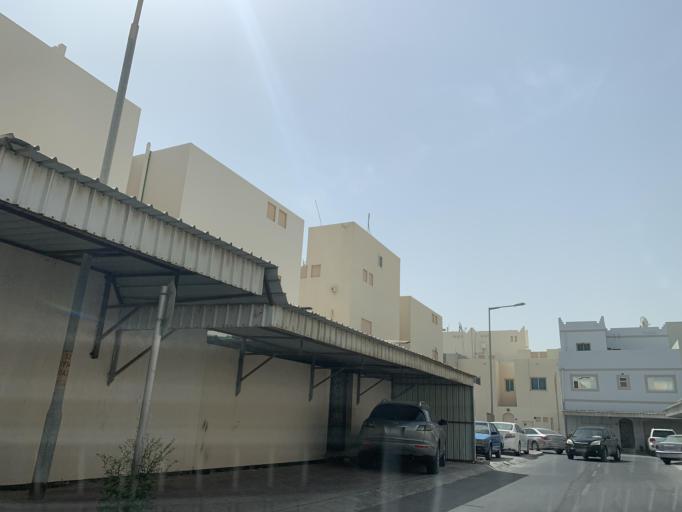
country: BH
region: Northern
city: Madinat `Isa
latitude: 26.1684
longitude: 50.5190
